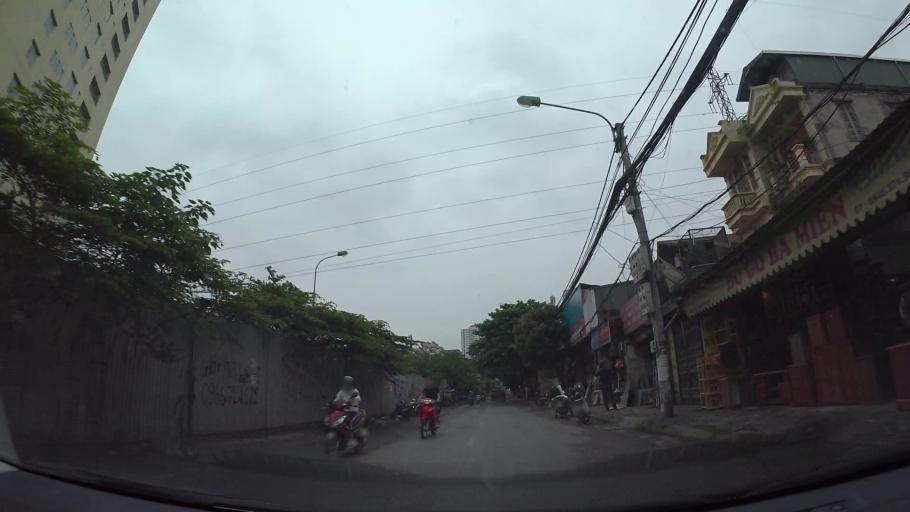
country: VN
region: Ha Noi
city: Hai BaTrung
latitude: 20.9861
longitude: 105.8697
